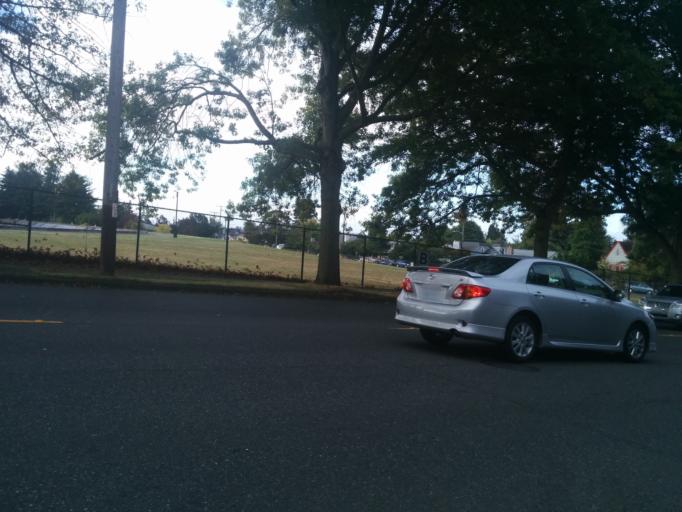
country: US
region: Washington
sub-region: King County
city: Shoreline
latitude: 47.6830
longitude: -122.3142
